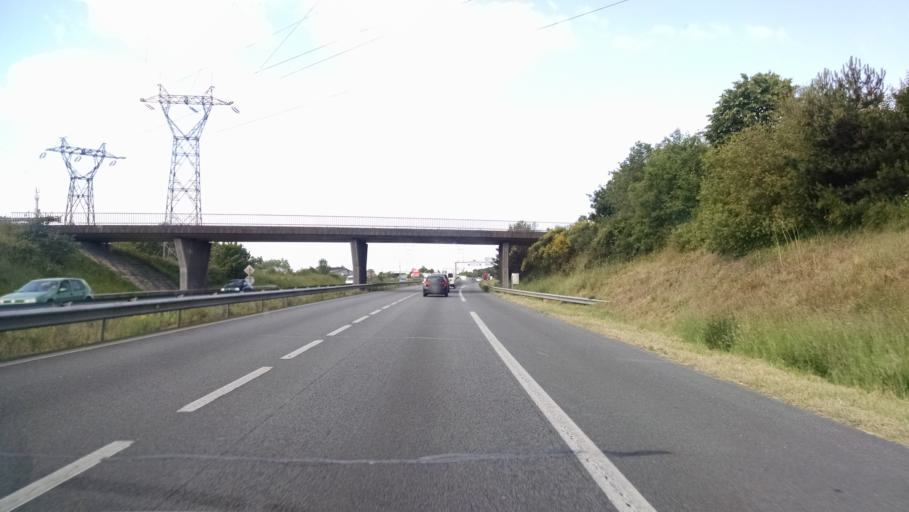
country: FR
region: Pays de la Loire
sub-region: Departement de la Loire-Atlantique
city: Les Sorinieres
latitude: 47.1601
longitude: -1.5343
